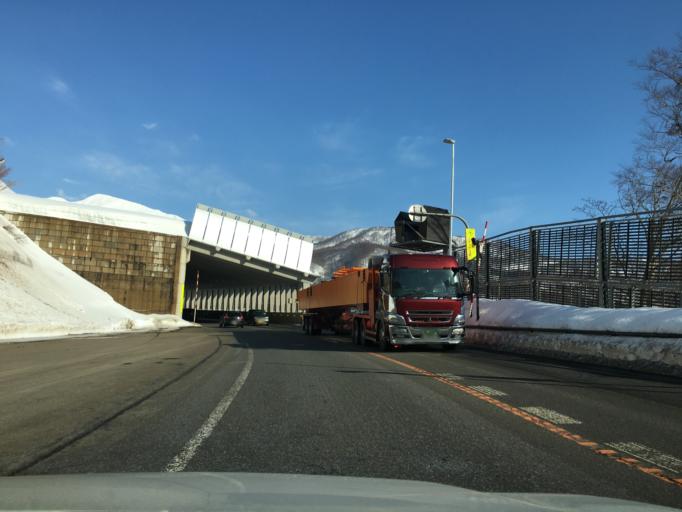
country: JP
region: Yamagata
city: Tsuruoka
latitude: 38.5319
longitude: 139.9406
